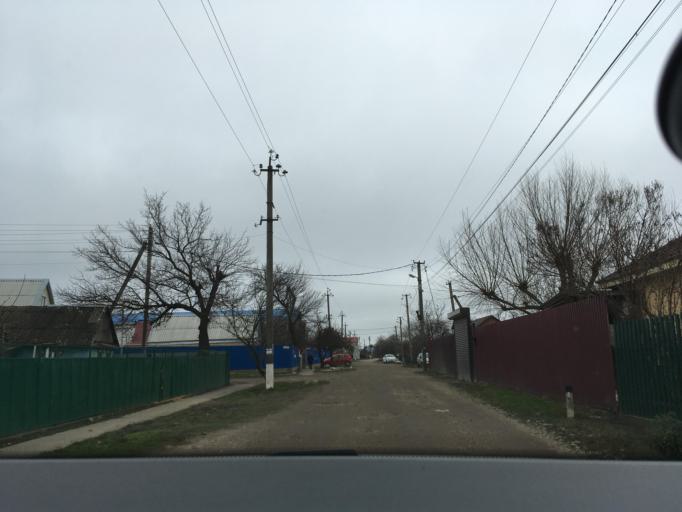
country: RU
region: Krasnodarskiy
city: Kushchevskaya
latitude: 46.5758
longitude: 39.6225
